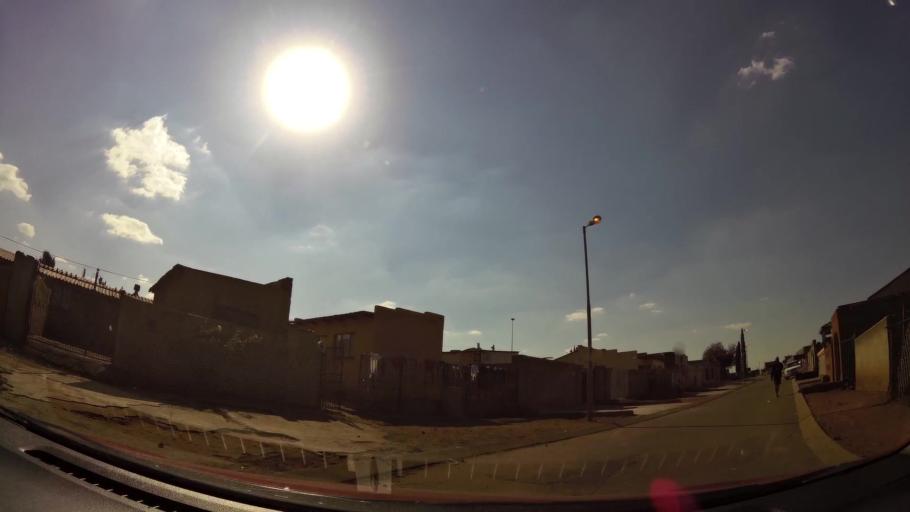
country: ZA
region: Gauteng
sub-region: City of Johannesburg Metropolitan Municipality
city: Soweto
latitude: -26.2358
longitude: 27.8797
